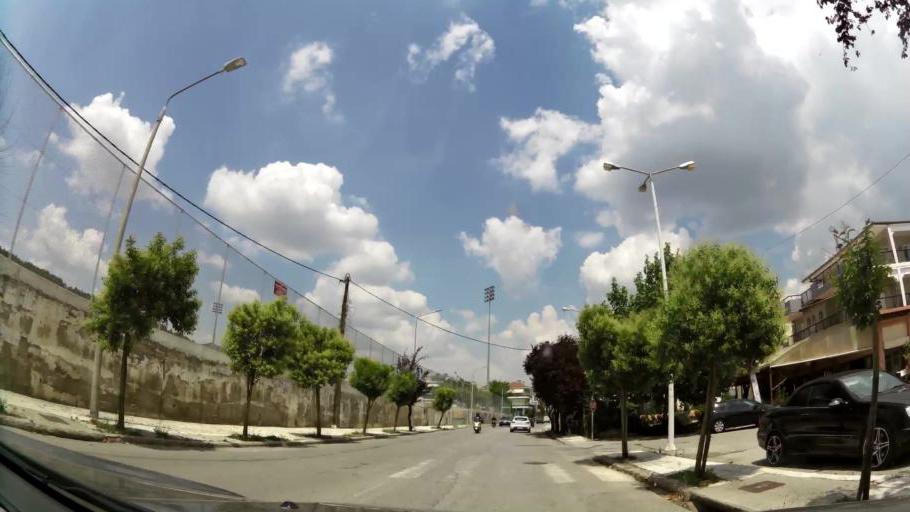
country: GR
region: West Macedonia
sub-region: Nomos Kozanis
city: Kozani
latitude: 40.2929
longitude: 21.7831
